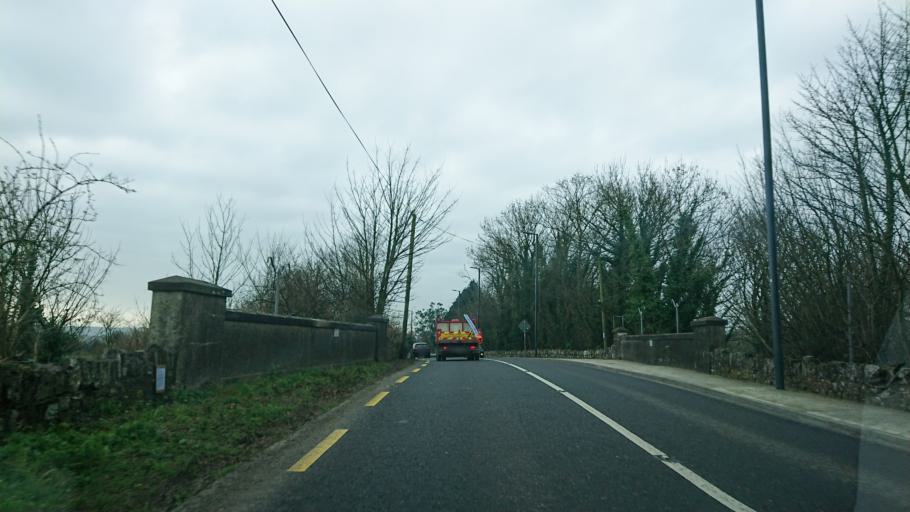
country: IE
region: Munster
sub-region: County Cork
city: Castlemartyr
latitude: 51.9383
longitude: -7.9966
